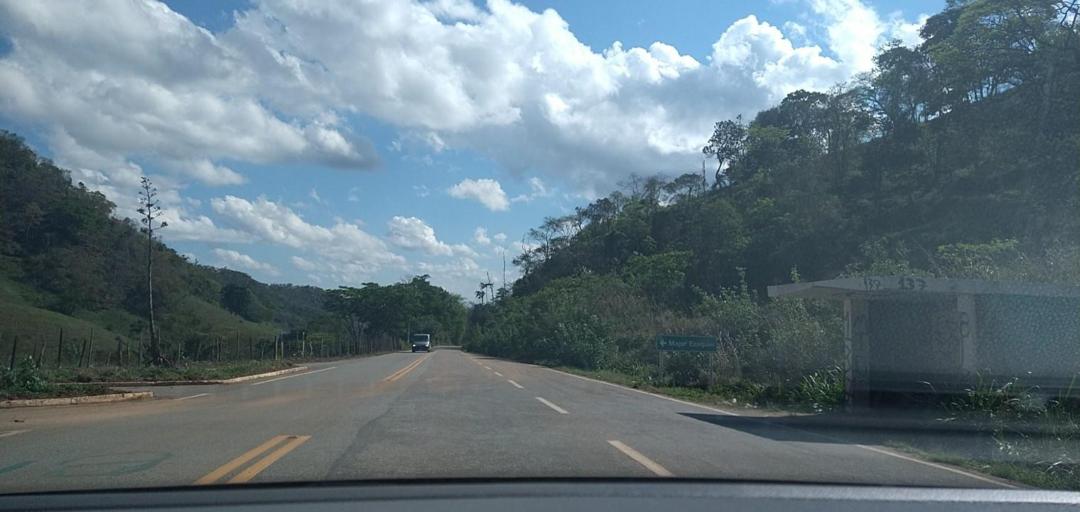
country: BR
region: Minas Gerais
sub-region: Alvinopolis
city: Alvinopolis
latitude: -20.0431
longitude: -43.0324
